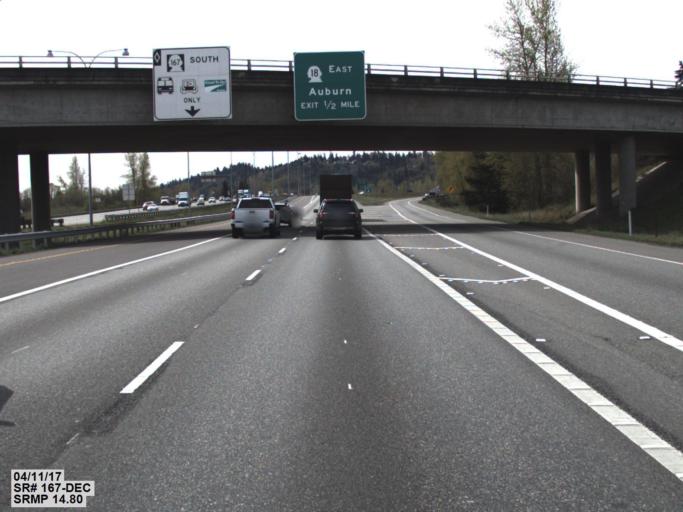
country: US
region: Washington
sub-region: King County
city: Auburn
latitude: 47.3088
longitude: -122.2487
